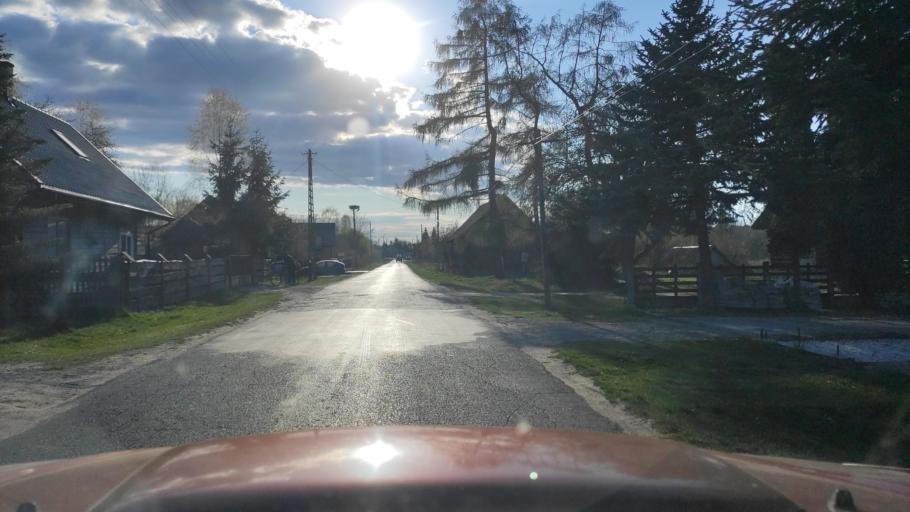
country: PL
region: Masovian Voivodeship
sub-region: Powiat zwolenski
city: Zwolen
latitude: 51.3844
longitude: 21.5652
